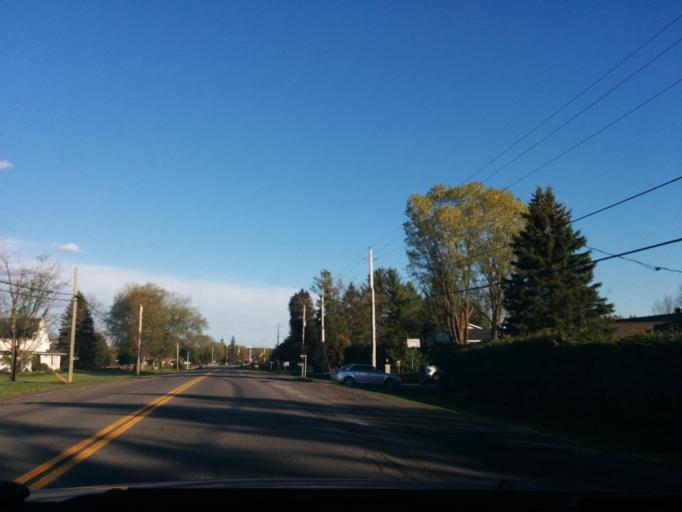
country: CA
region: Ontario
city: Ottawa
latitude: 45.2050
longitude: -75.6424
